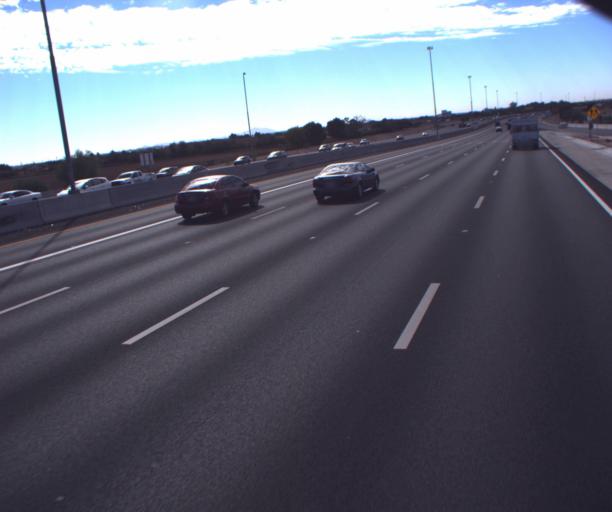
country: US
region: Arizona
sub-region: Maricopa County
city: Scottsdale
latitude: 33.4924
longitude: -111.8881
